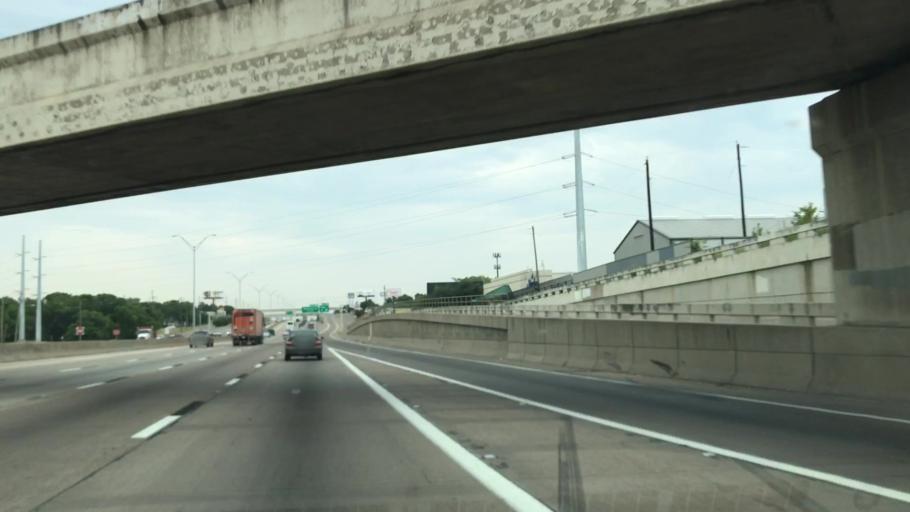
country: US
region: Texas
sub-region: Tarrant County
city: Fort Worth
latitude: 32.7037
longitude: -97.3208
